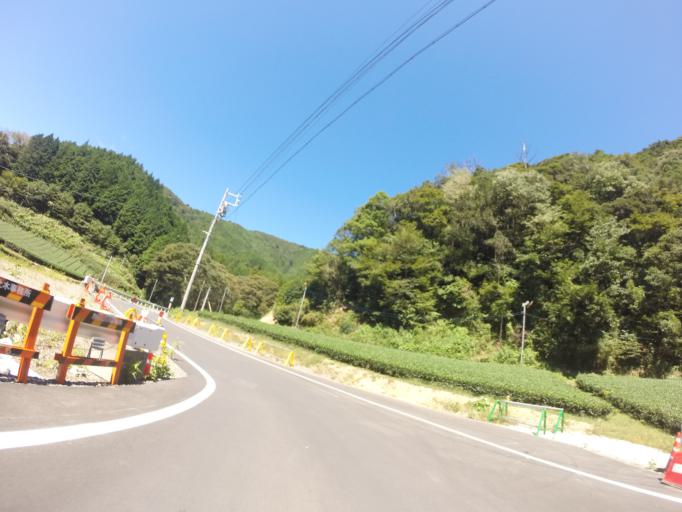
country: JP
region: Shizuoka
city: Fujieda
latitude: 34.9676
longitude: 138.1920
